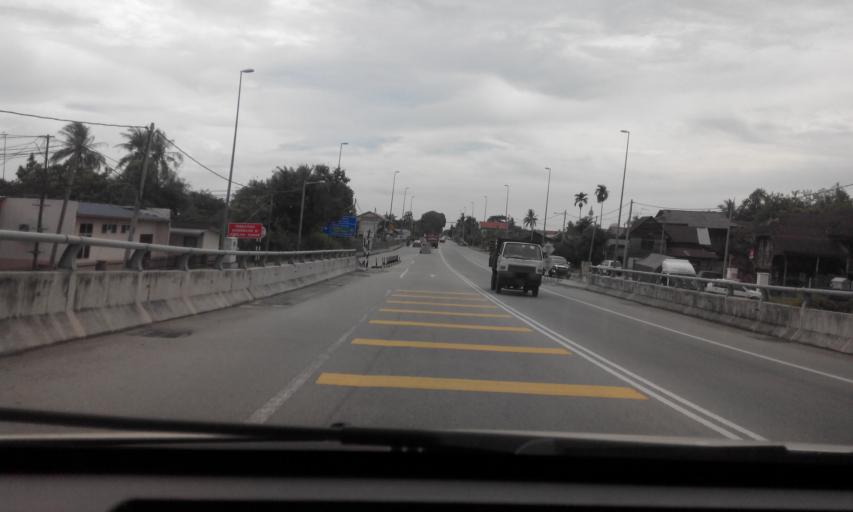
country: MY
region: Perak
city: Parit Buntar
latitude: 5.1318
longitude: 100.4834
